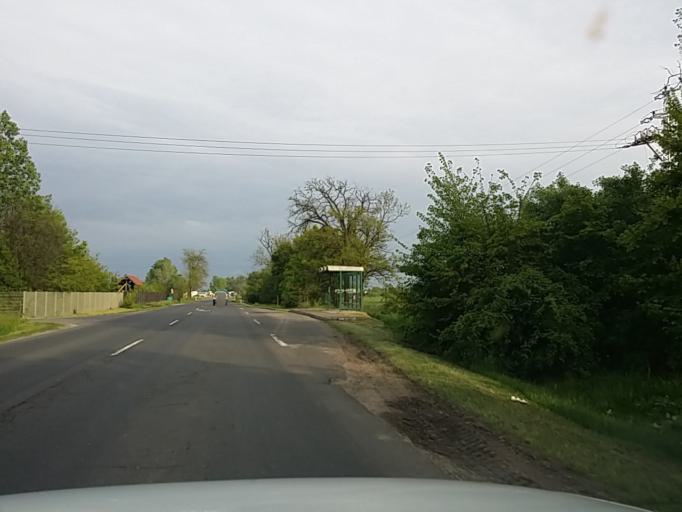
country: HU
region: Jasz-Nagykun-Szolnok
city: Jaszbereny
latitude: 47.5181
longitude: 19.8751
